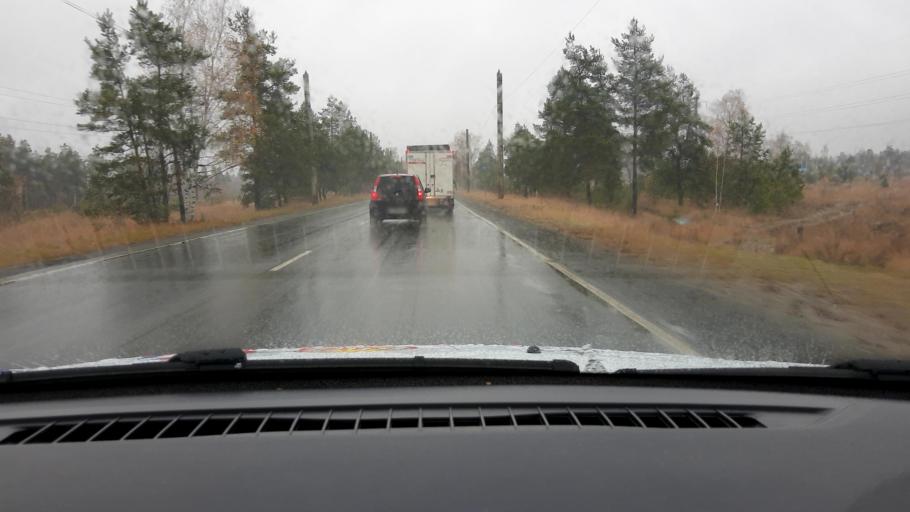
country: RU
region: Nizjnij Novgorod
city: Babino
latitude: 56.2815
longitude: 43.5724
